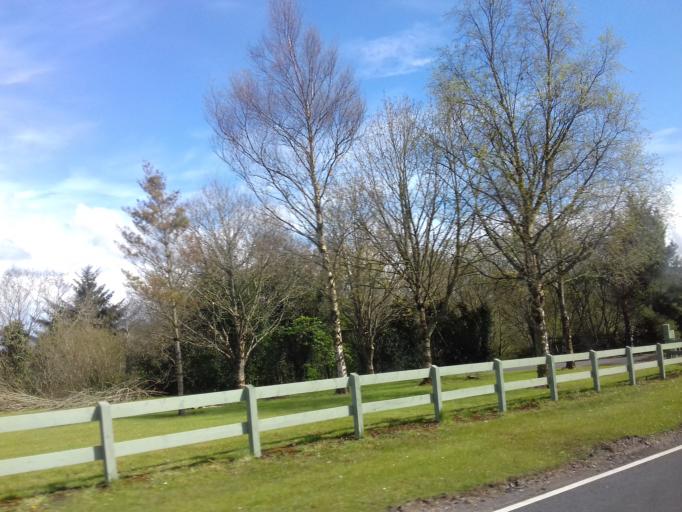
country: GB
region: Northern Ireland
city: Irvinestown
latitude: 54.4464
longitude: -7.7941
